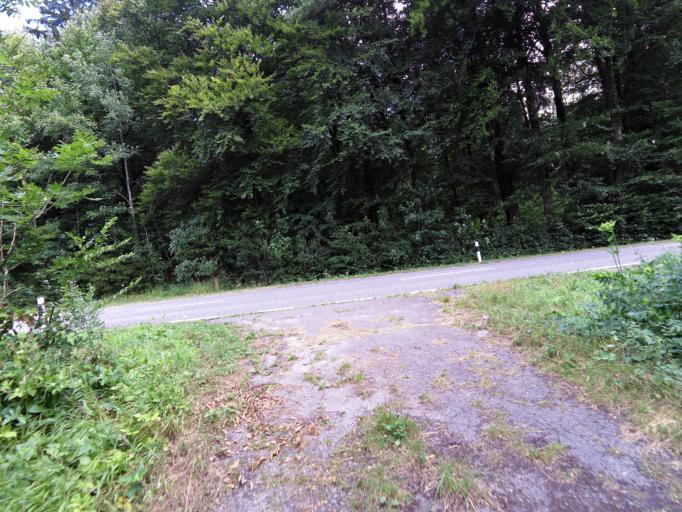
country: CH
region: Thurgau
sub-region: Kreuzlingen District
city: Tagerwilen
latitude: 47.6457
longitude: 9.1032
